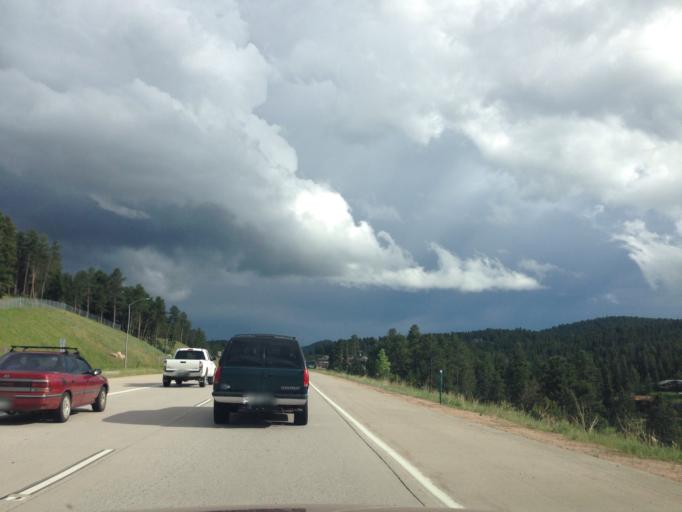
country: US
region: Colorado
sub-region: Jefferson County
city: Evergreen
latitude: 39.5262
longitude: -105.3073
